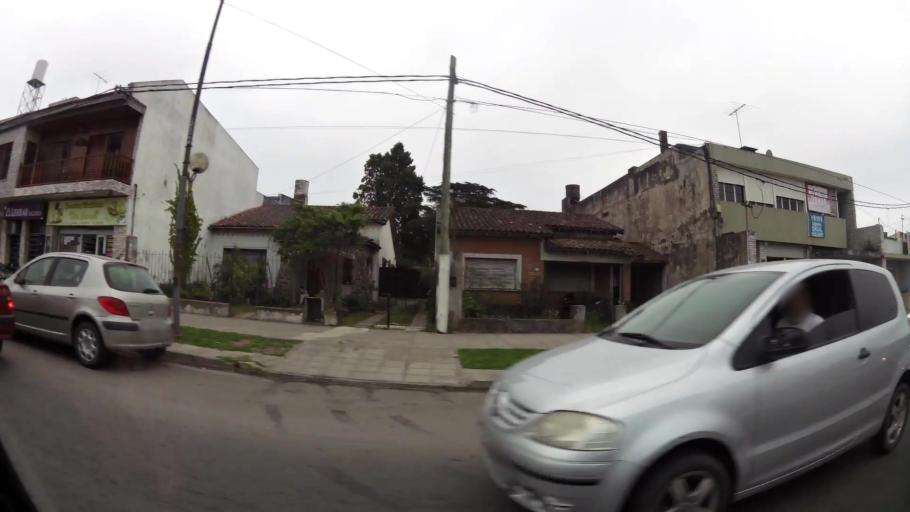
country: AR
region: Buenos Aires
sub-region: Partido de La Plata
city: La Plata
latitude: -34.9239
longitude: -57.9944
